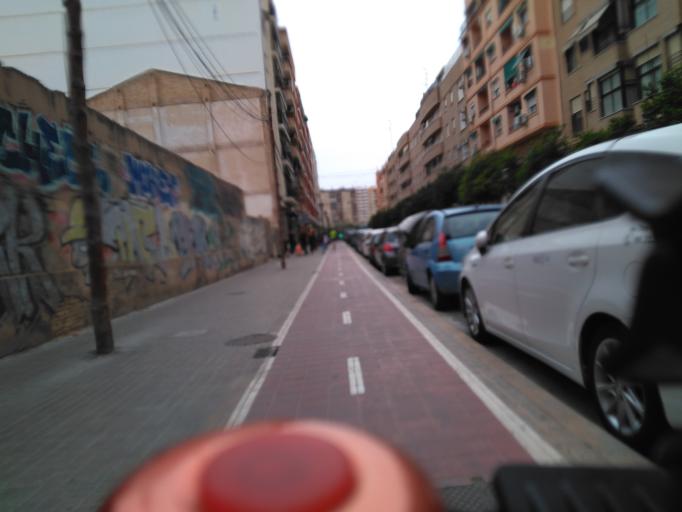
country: ES
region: Valencia
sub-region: Provincia de Valencia
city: Mislata
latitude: 39.4722
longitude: -0.3990
